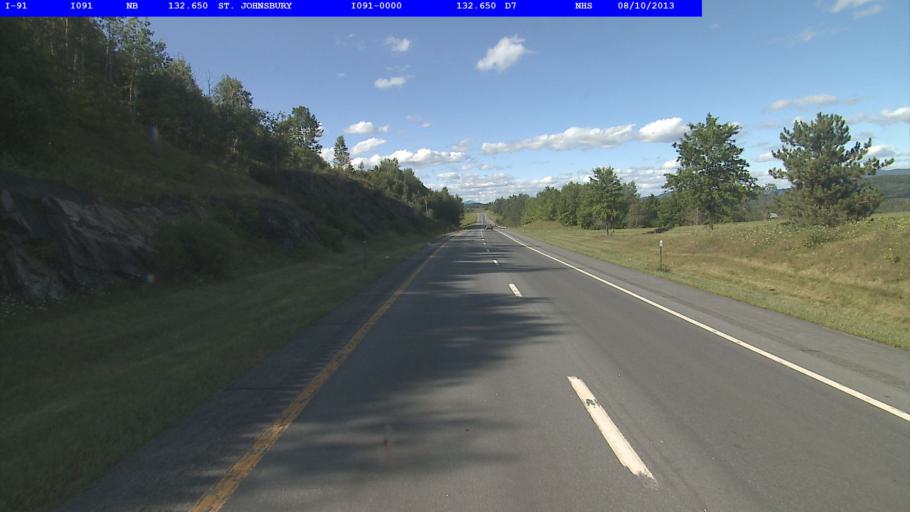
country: US
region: Vermont
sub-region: Caledonia County
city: St Johnsbury
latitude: 44.4552
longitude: -72.0243
